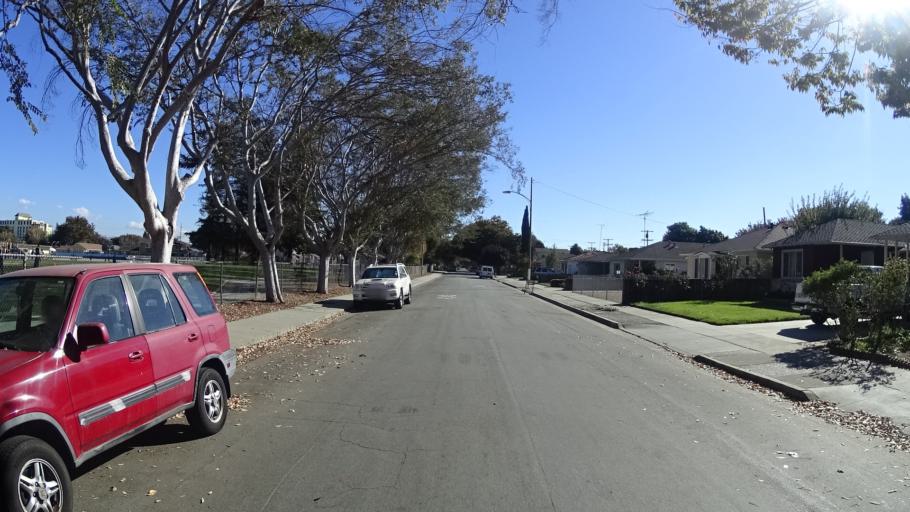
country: US
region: California
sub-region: Santa Clara County
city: San Jose
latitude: 37.3621
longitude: -121.9141
